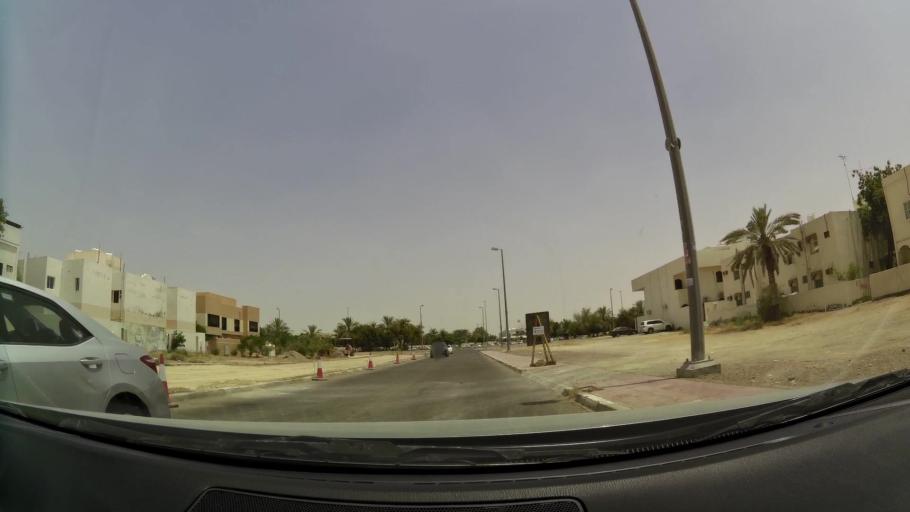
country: AE
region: Abu Dhabi
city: Al Ain
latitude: 24.2045
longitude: 55.7197
